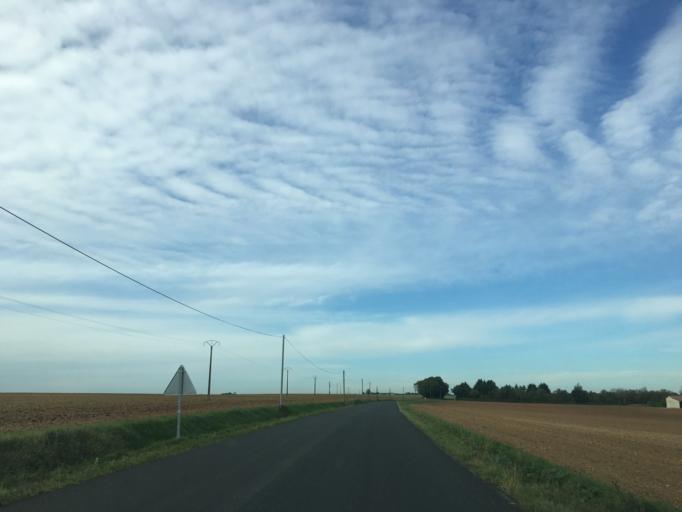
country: FR
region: Poitou-Charentes
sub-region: Departement des Deux-Sevres
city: Beauvoir-sur-Niort
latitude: 46.0679
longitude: -0.4758
